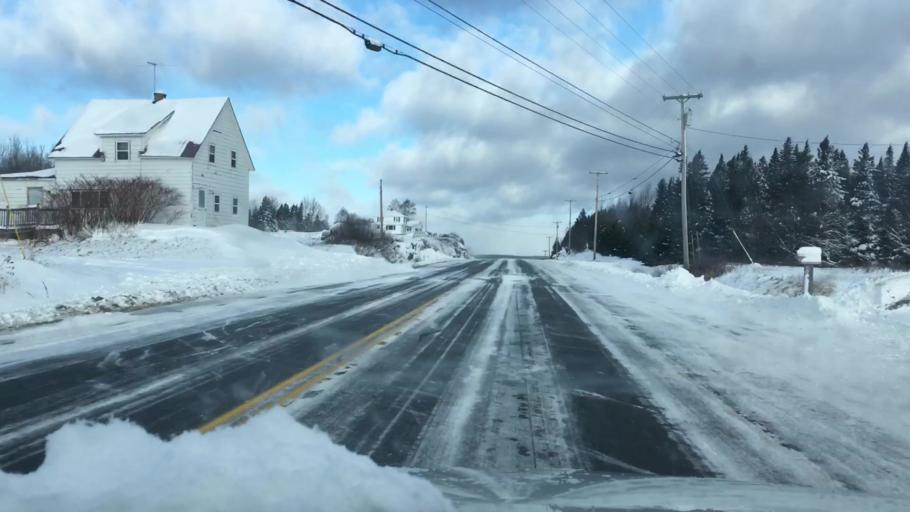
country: US
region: Maine
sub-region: Aroostook County
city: Caribou
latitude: 46.9642
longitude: -68.0325
